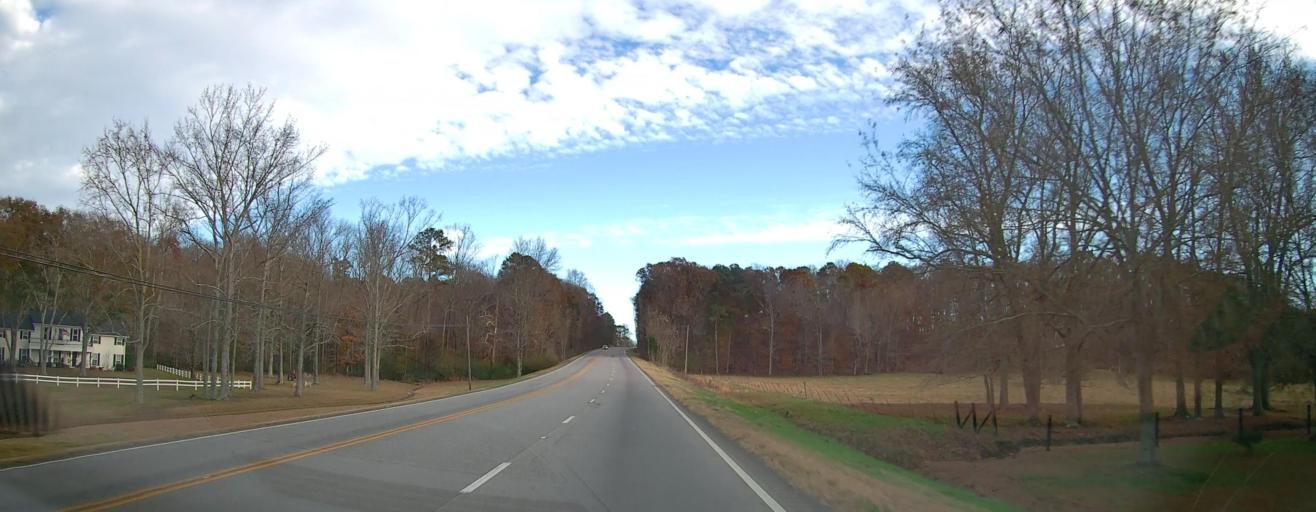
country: US
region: Alabama
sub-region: Marshall County
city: Arab
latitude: 34.3555
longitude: -86.6231
